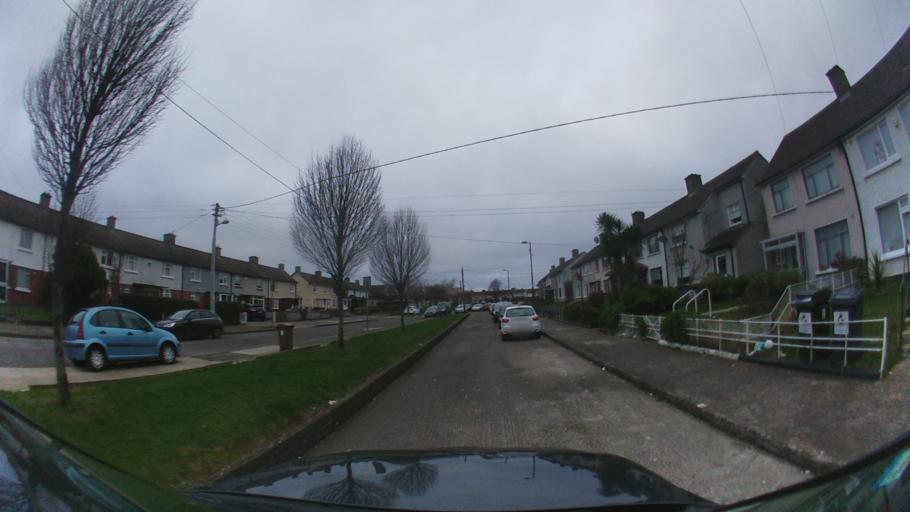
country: IE
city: Coolock
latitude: 53.3843
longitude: -6.1988
